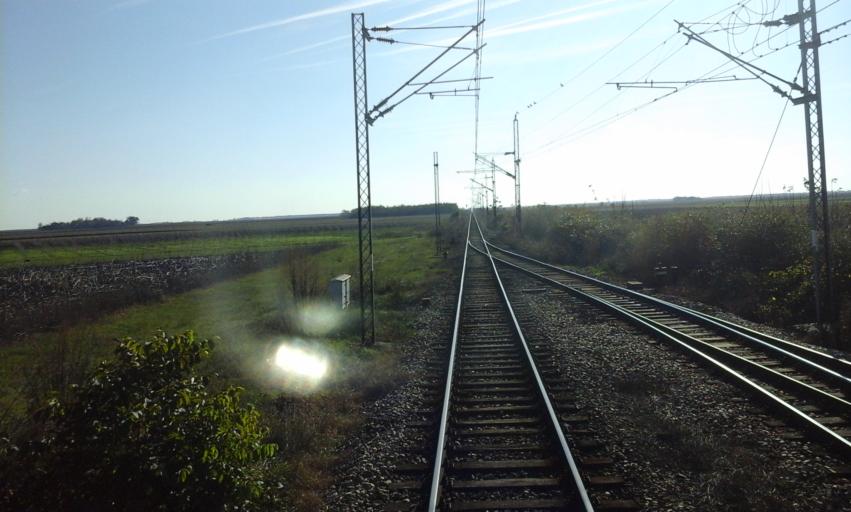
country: RS
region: Autonomna Pokrajina Vojvodina
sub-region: Severnobacki Okrug
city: Backa Topola
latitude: 45.9337
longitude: 19.6674
